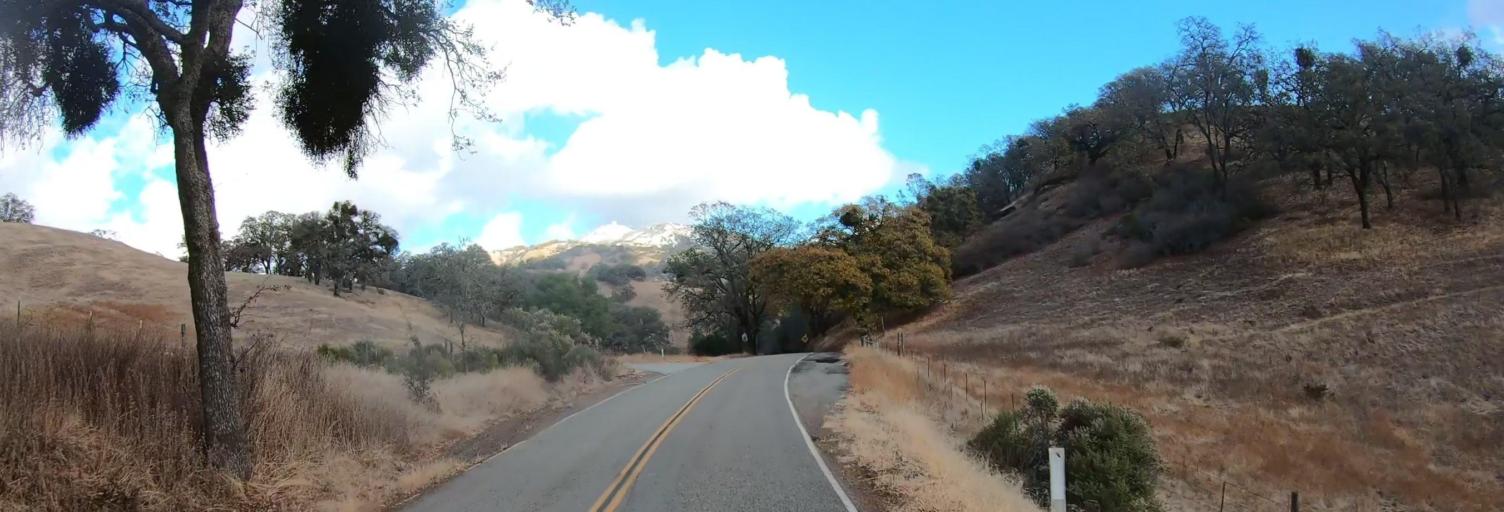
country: US
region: California
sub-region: Santa Clara County
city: East Foothills
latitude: 37.3288
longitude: -121.6816
